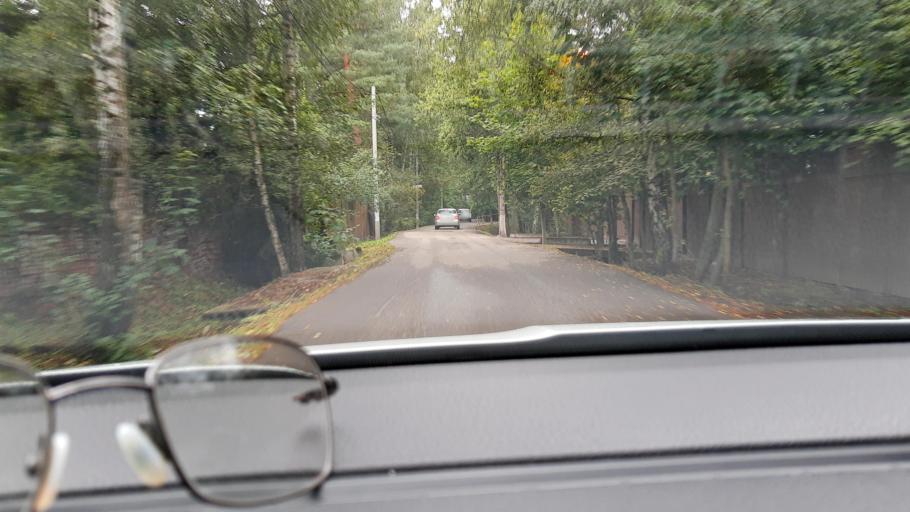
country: RU
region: Moskovskaya
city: Kokoshkino
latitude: 55.5919
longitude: 37.1670
